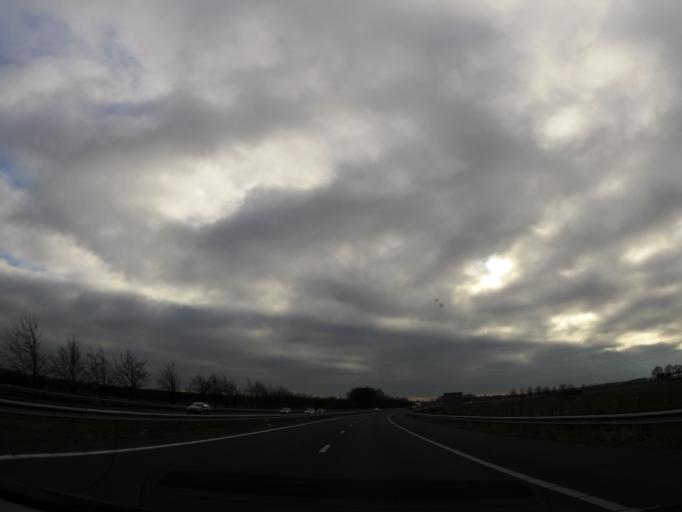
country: NL
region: Limburg
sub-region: Gemeente Beesel
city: Offenbeek
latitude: 51.2773
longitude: 6.1006
